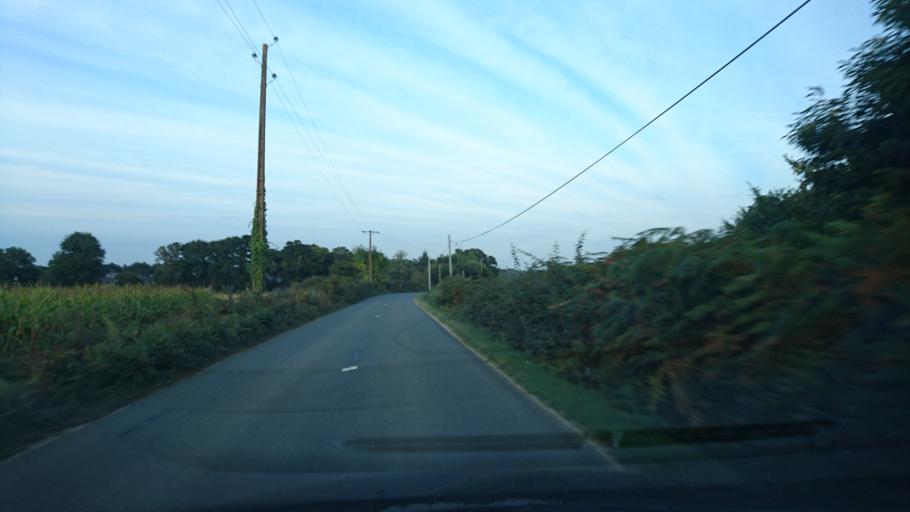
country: FR
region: Brittany
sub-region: Departement d'Ille-et-Vilaine
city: Sixt-sur-Aff
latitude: 47.8110
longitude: -2.0425
